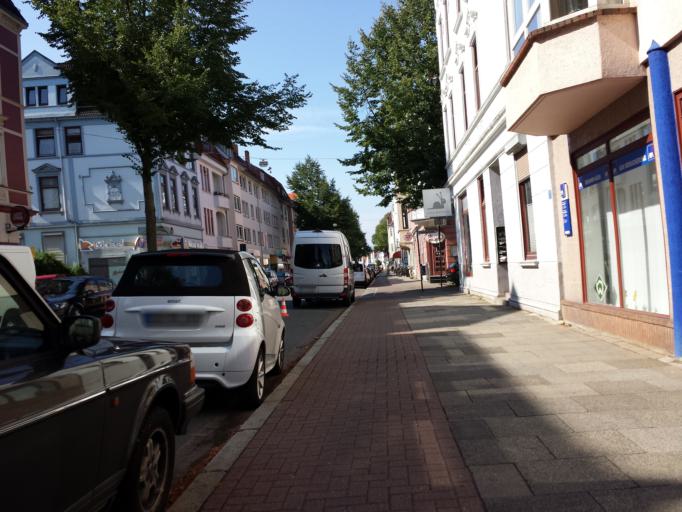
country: DE
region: Bremen
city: Bremen
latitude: 53.0626
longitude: 8.8039
